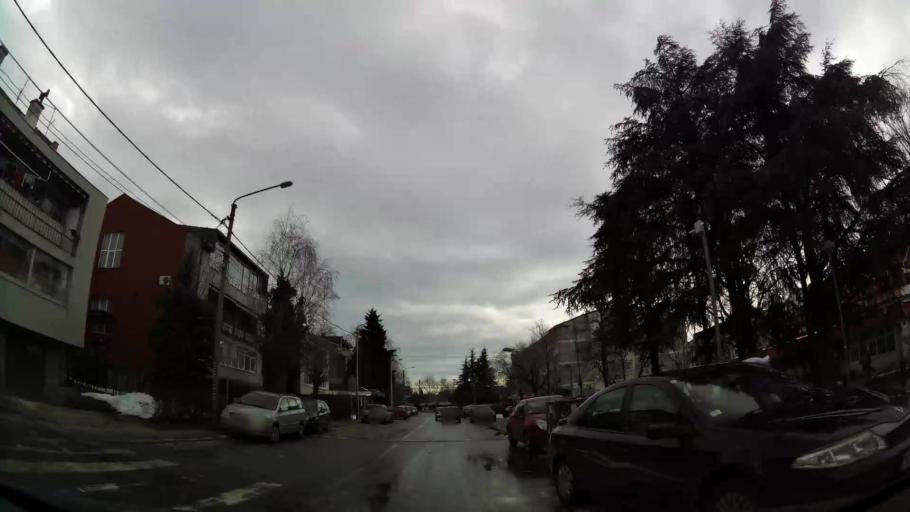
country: RS
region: Central Serbia
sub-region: Belgrade
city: Rakovica
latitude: 44.7498
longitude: 20.4173
